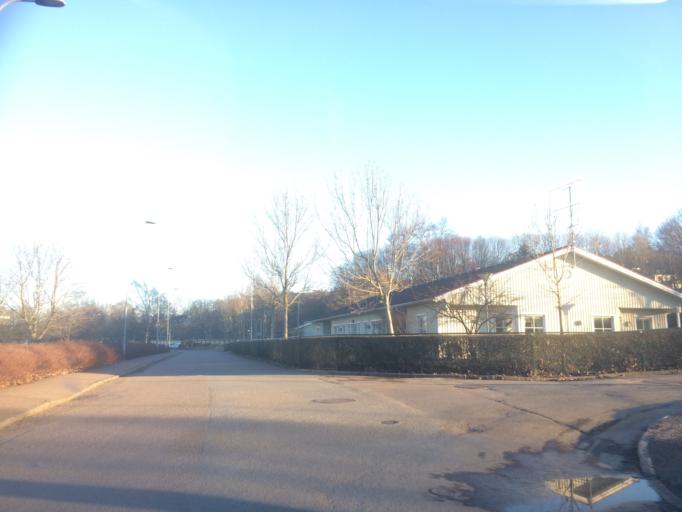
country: SE
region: Vaestra Goetaland
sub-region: Goteborg
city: Goeteborg
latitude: 57.7503
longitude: 11.9315
